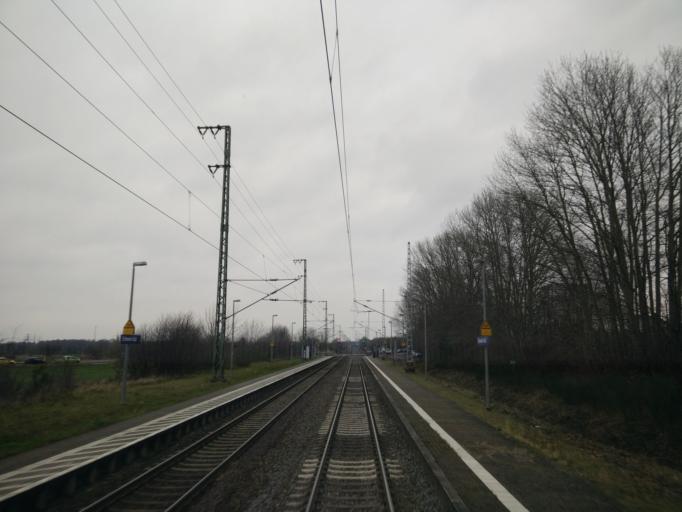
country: DE
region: Mecklenburg-Vorpommern
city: Klein Rogahn
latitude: 53.5739
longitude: 11.3765
